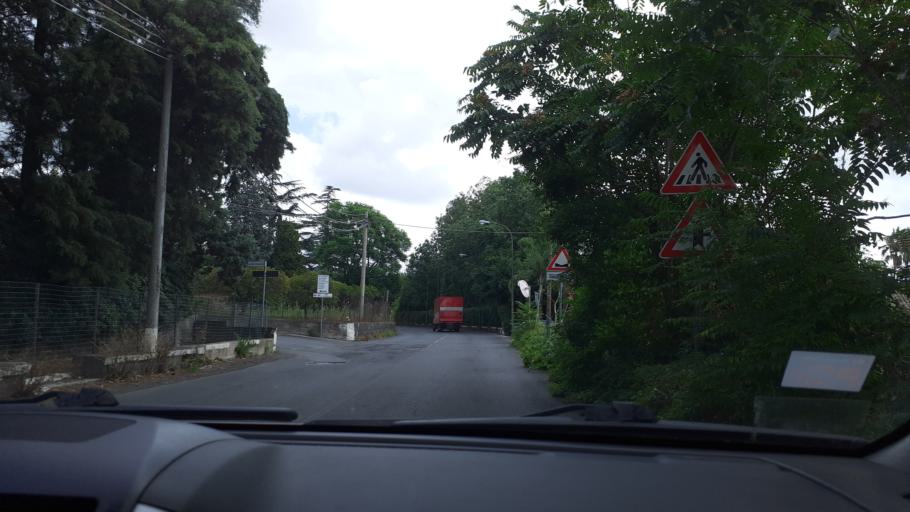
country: IT
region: Sicily
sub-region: Catania
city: Carrubazza-Motta
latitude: 37.5523
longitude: 15.1057
